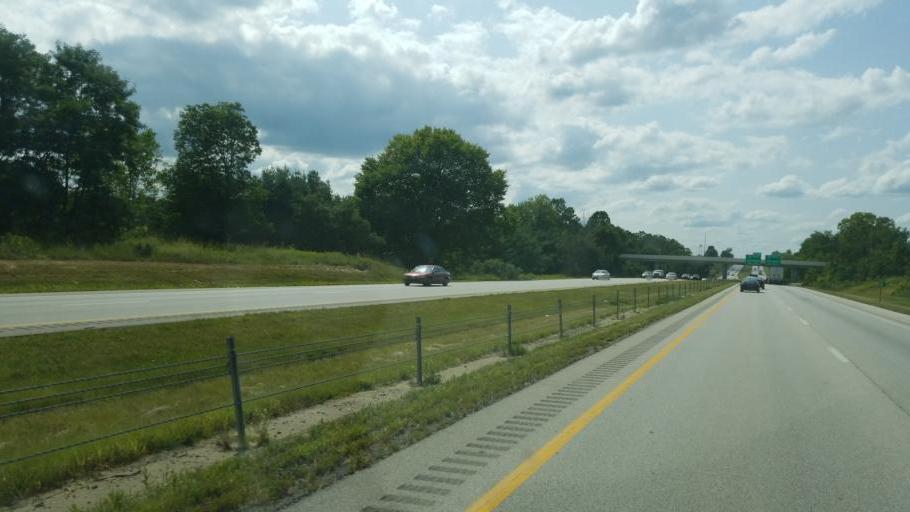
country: US
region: Ohio
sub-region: Medina County
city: Seville
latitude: 41.0328
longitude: -81.8467
